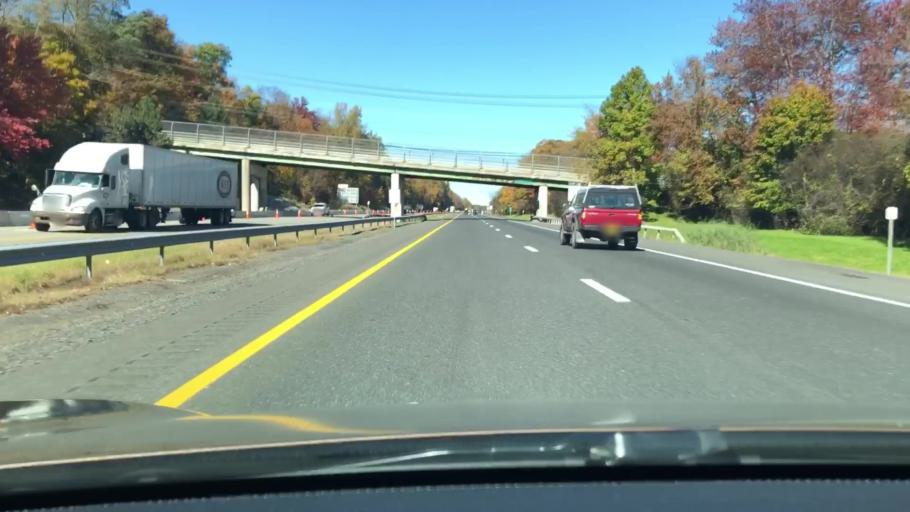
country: US
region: New York
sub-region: Orange County
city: Gardnertown
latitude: 41.5215
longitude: -74.0742
